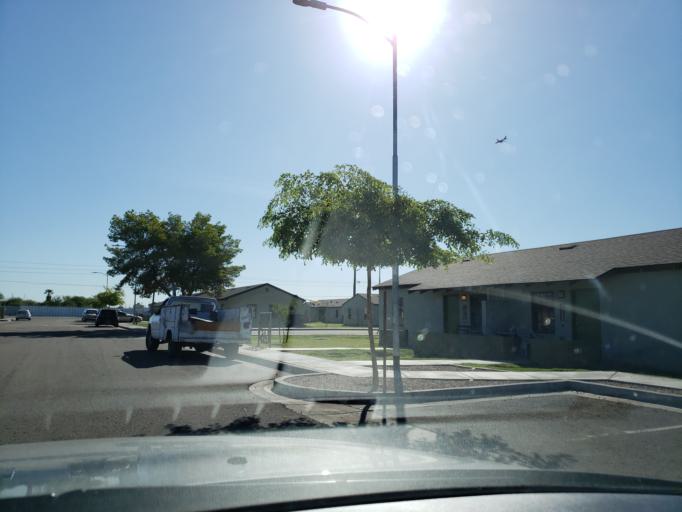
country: US
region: Arizona
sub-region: Maricopa County
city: Phoenix
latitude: 33.4355
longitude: -112.1012
